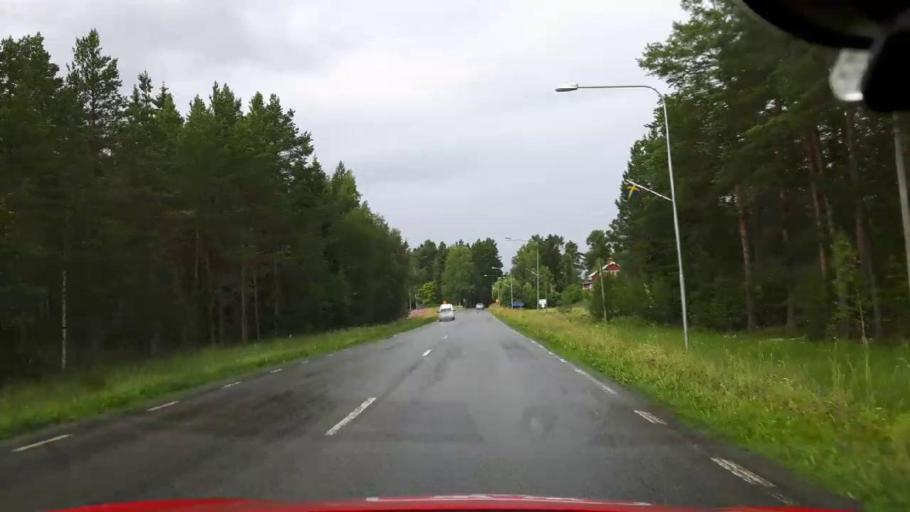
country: SE
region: Jaemtland
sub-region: Krokoms Kommun
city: Krokom
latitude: 63.3453
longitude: 14.2621
